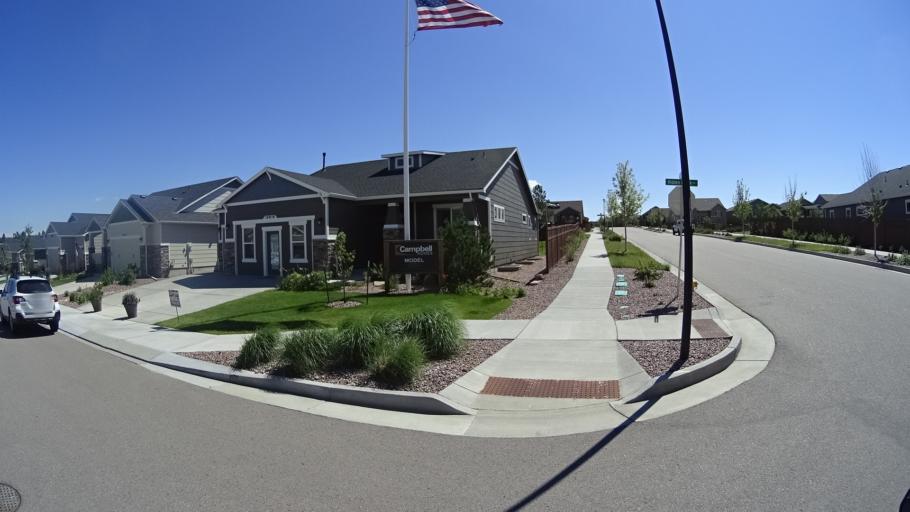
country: US
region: Colorado
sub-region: El Paso County
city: Black Forest
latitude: 38.9901
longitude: -104.7613
